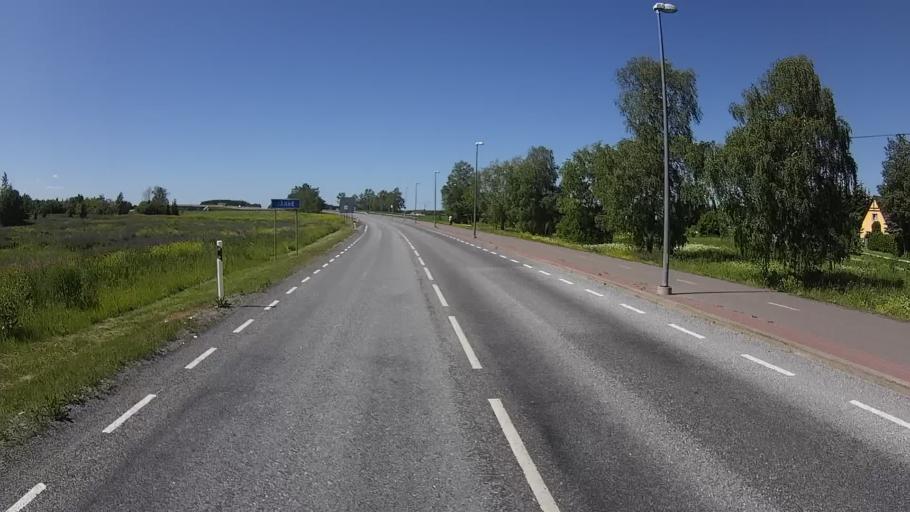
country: EE
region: Ida-Virumaa
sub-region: Kohtla-Jaerve linn
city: Kohtla-Jarve
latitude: 59.4013
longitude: 27.3371
